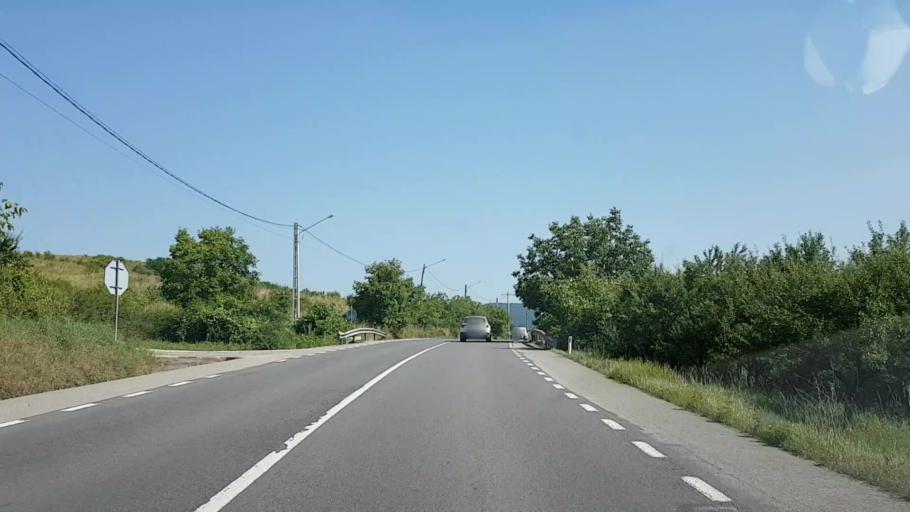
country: RO
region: Bistrita-Nasaud
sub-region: Comuna Sieu-Magherus
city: Sieu-Magherus
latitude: 47.0773
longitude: 24.3971
